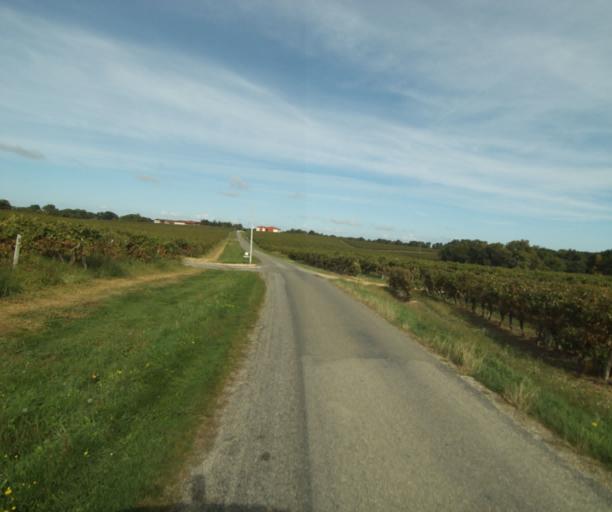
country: FR
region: Midi-Pyrenees
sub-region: Departement du Gers
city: Eauze
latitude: 43.8541
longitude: 0.1389
